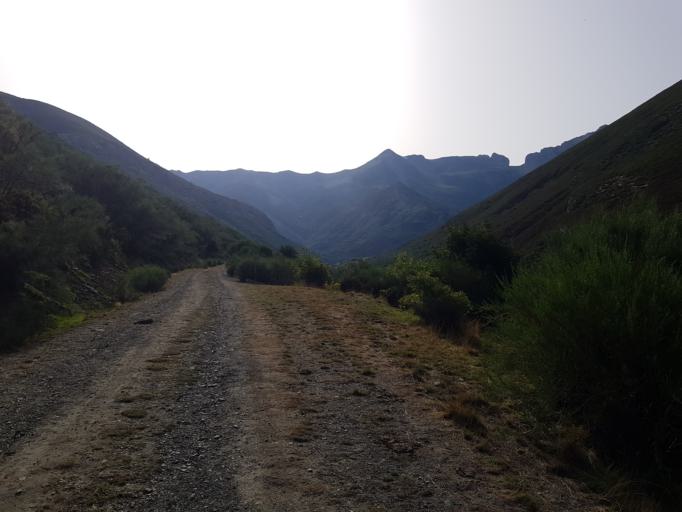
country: ES
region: Asturias
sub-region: Province of Asturias
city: Rio Aller
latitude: 43.0118
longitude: -5.4632
